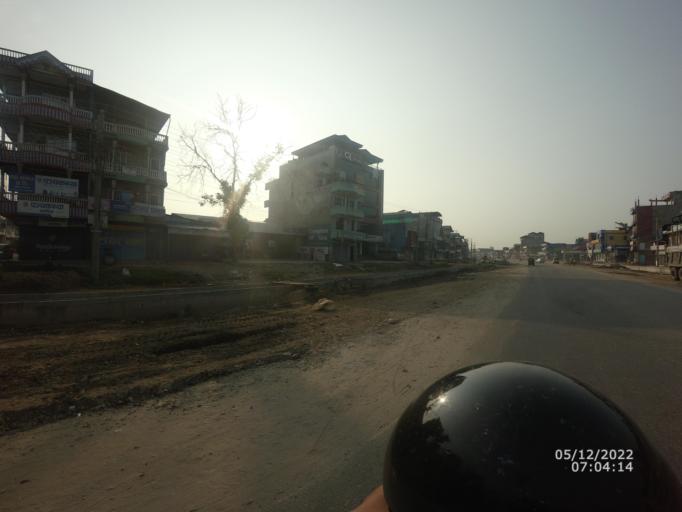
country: NP
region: Central Region
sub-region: Narayani Zone
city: Bharatpur
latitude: 27.6728
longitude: 84.4329
